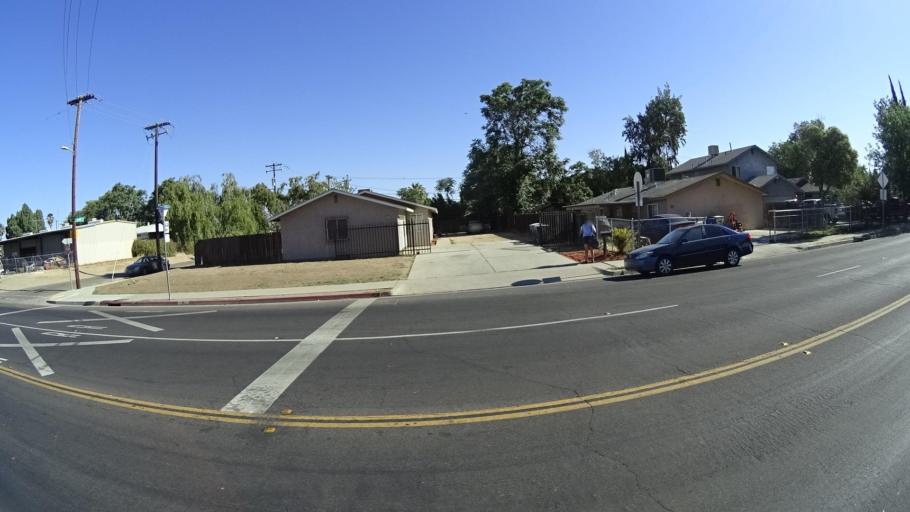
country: US
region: California
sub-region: Fresno County
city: Fresno
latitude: 36.7577
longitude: -119.7856
